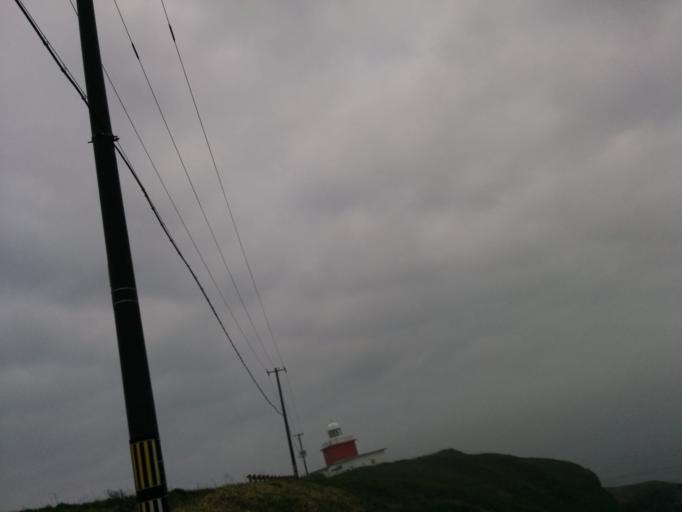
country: JP
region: Hokkaido
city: Nemuro
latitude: 43.0776
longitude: 145.1664
